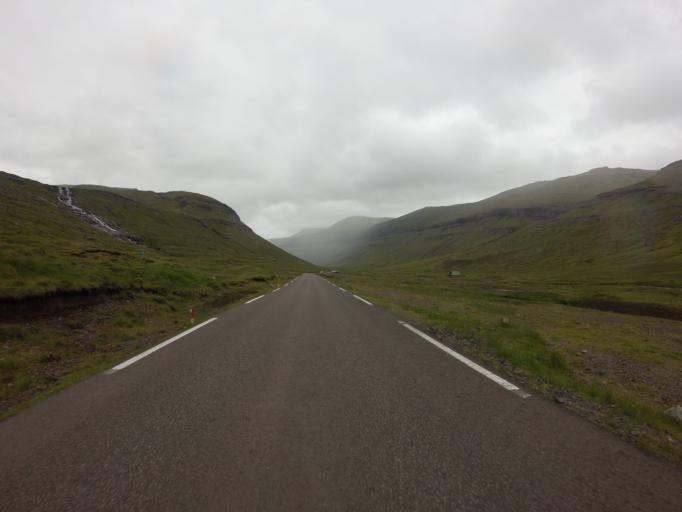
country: FO
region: Streymoy
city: Vestmanna
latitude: 62.2206
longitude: -7.1271
